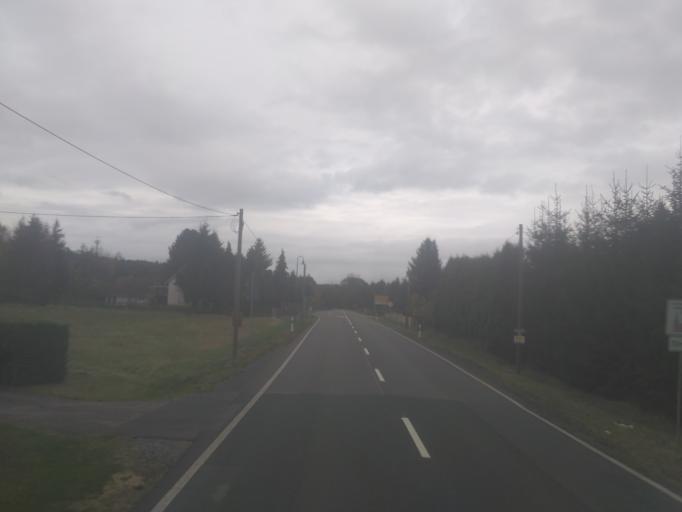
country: DE
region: Brandenburg
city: Merzdorf
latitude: 51.3871
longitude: 13.5110
